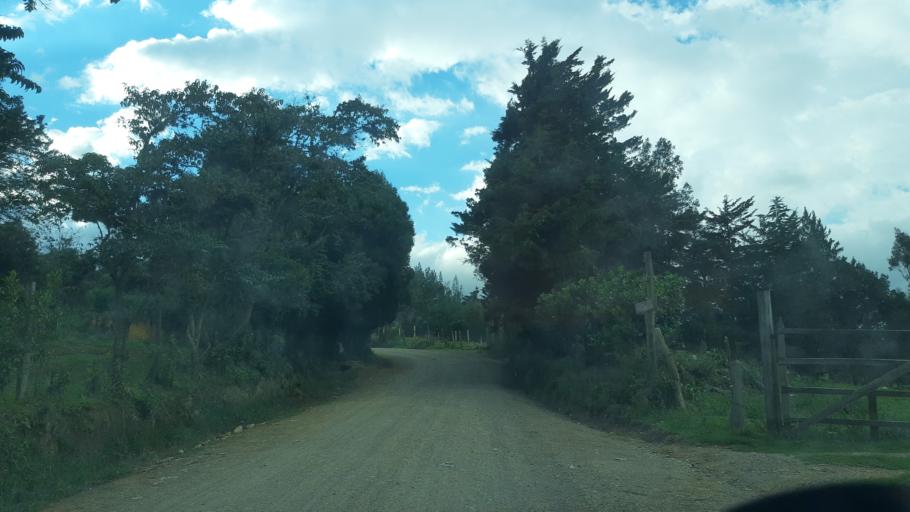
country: CO
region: Boyaca
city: Santa Sofia
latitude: 5.7312
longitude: -73.5963
